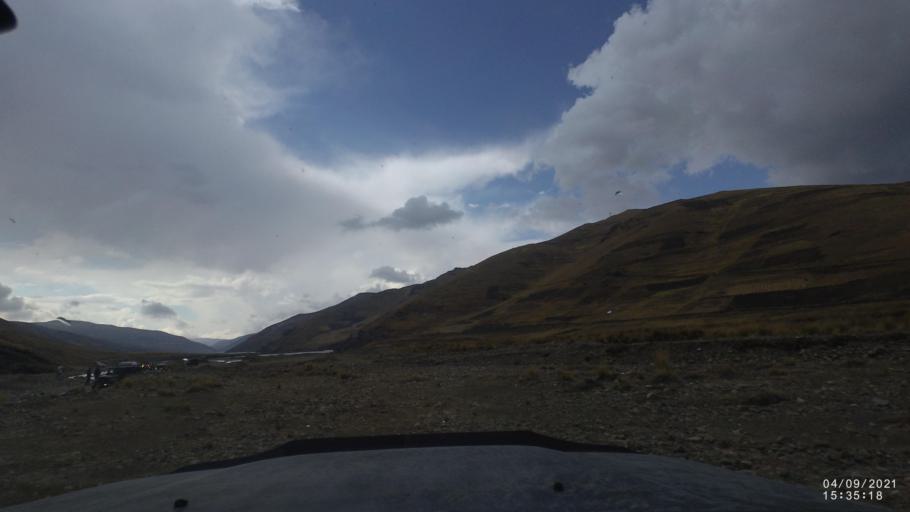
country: BO
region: Cochabamba
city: Cochabamba
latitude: -17.1543
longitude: -66.3115
